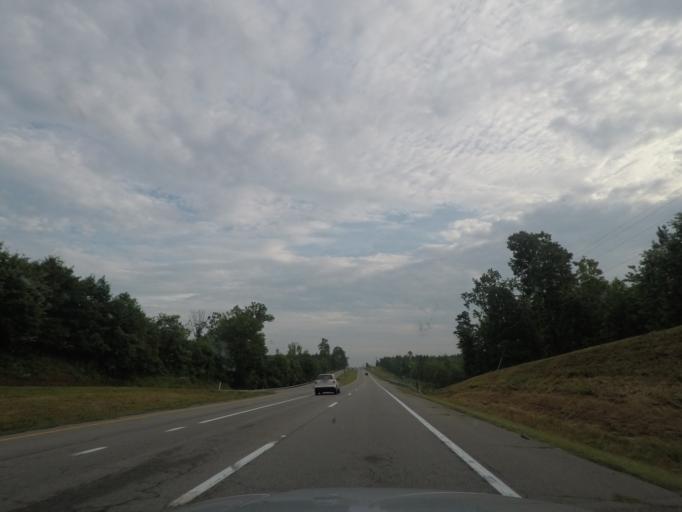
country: US
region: Virginia
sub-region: Halifax County
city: South Boston
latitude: 36.6760
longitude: -78.8974
